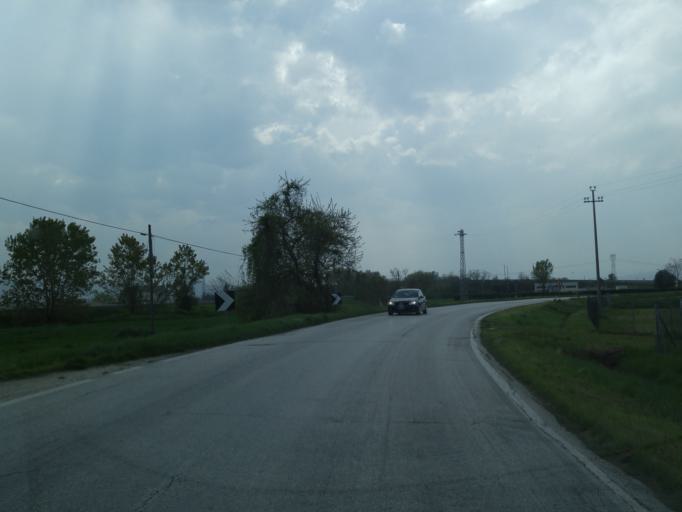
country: IT
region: The Marches
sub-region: Provincia di Pesaro e Urbino
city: Bellocchi
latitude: 43.7797
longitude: 12.9839
